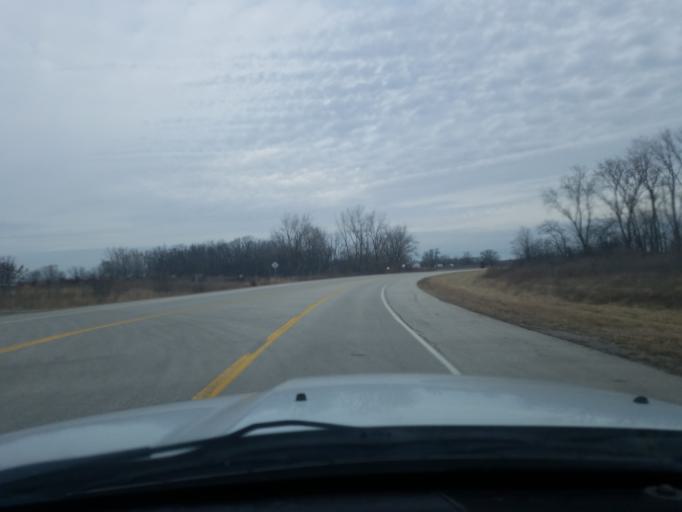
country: US
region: Indiana
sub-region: Huntington County
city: Roanoke
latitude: 40.9932
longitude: -85.2616
